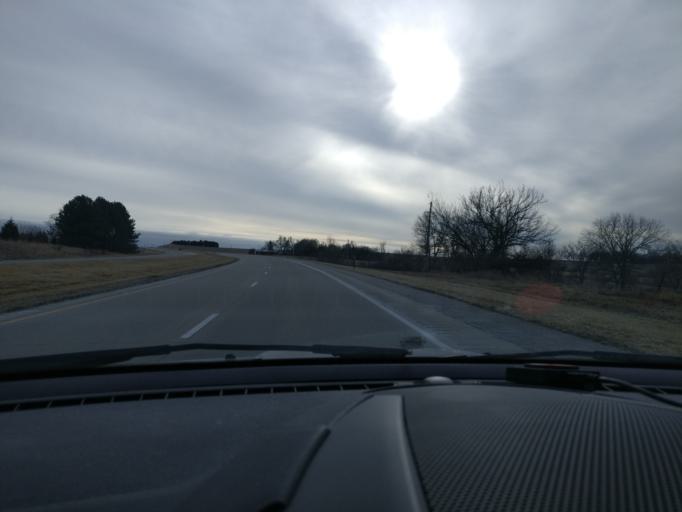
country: US
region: Nebraska
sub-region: Saunders County
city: Wahoo
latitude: 41.0946
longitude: -96.6395
